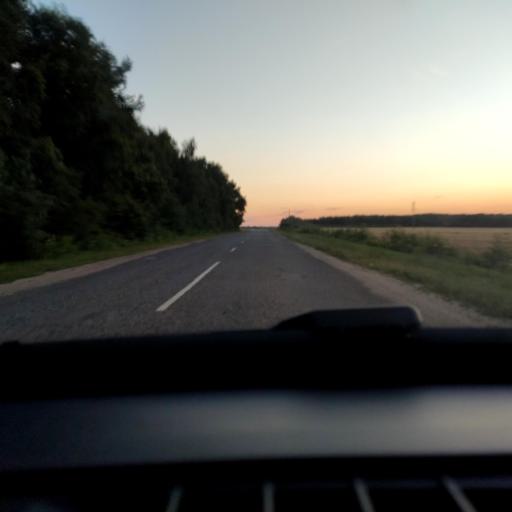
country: RU
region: Lipetsk
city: Zadonsk
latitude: 52.3100
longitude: 38.8883
